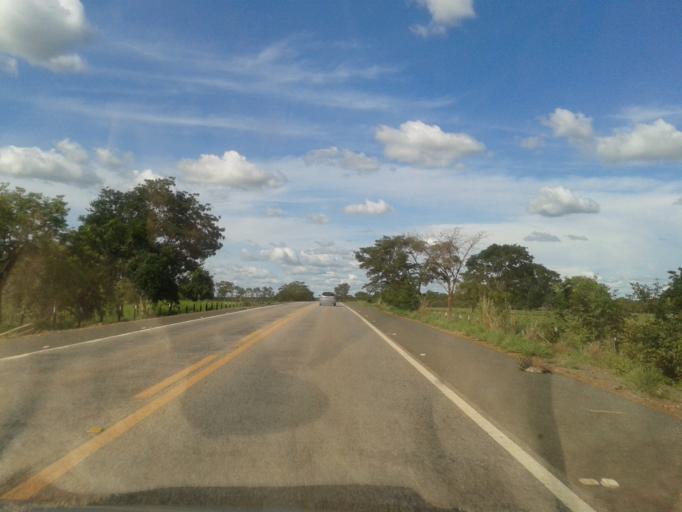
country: BR
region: Goias
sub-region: Mozarlandia
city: Mozarlandia
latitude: -15.0131
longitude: -50.5941
